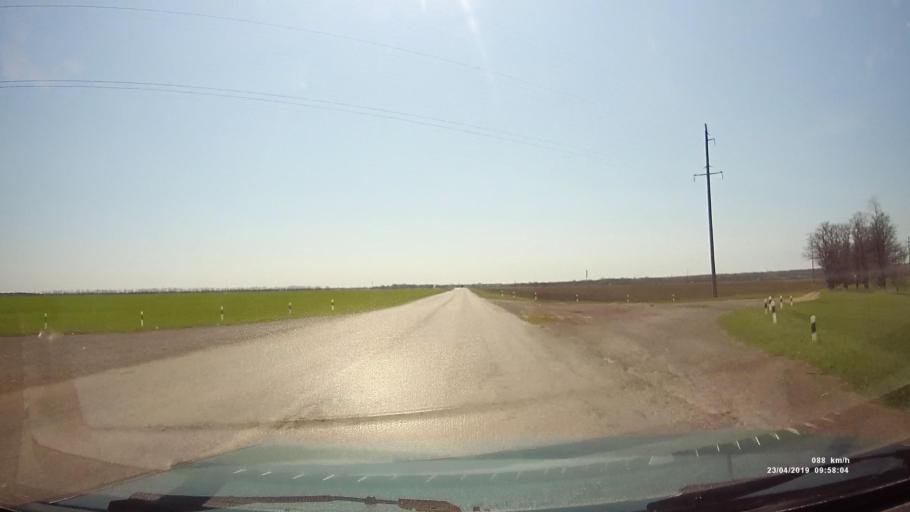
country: RU
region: Rostov
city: Sovetskoye
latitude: 46.7829
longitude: 42.0942
